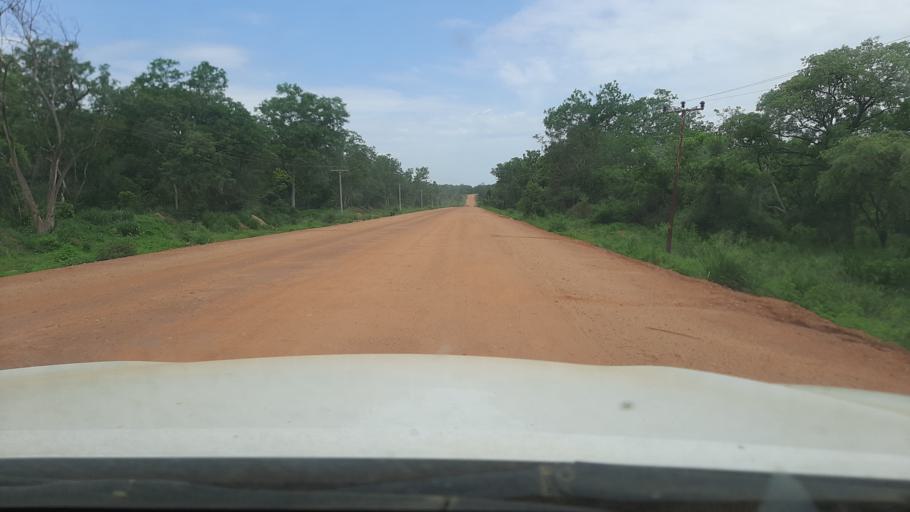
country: ET
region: Gambela
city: Gambela
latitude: 8.0960
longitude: 34.5880
